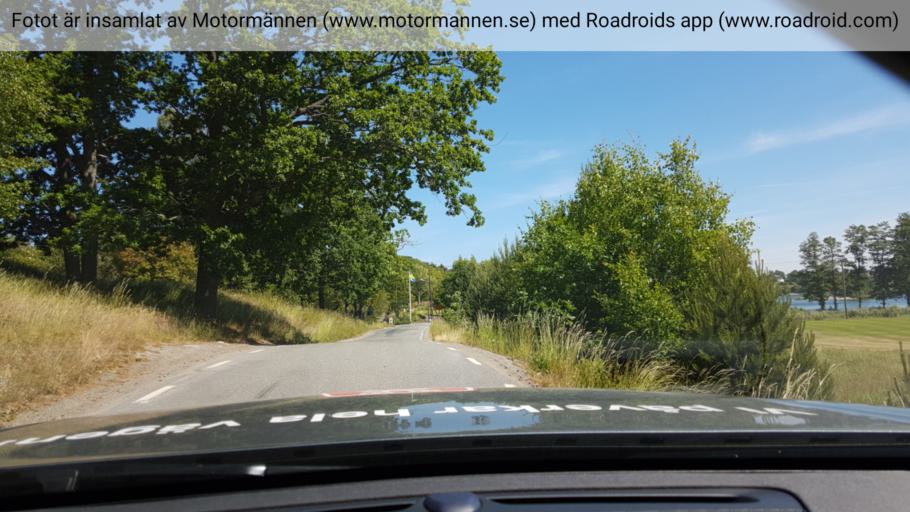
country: SE
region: Stockholm
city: Dalaro
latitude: 59.1649
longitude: 18.4502
